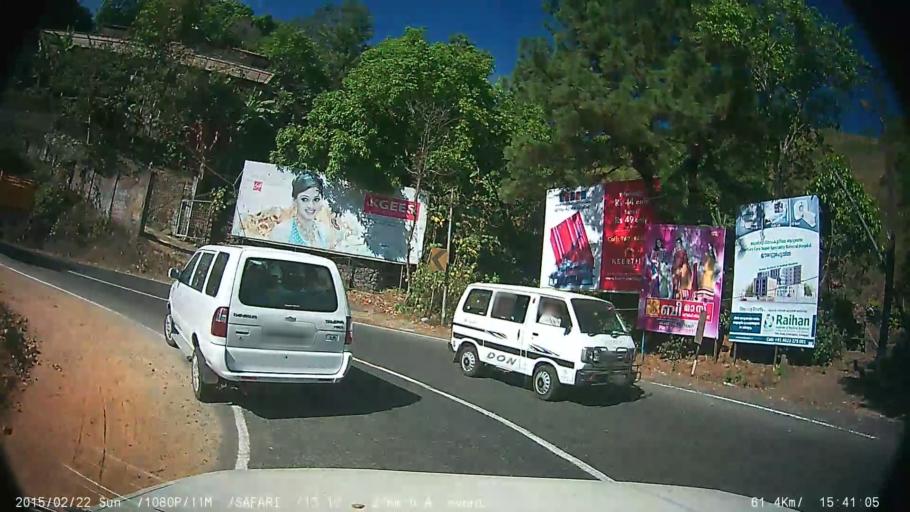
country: IN
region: Kerala
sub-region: Kottayam
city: Erattupetta
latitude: 9.5734
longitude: 76.9757
